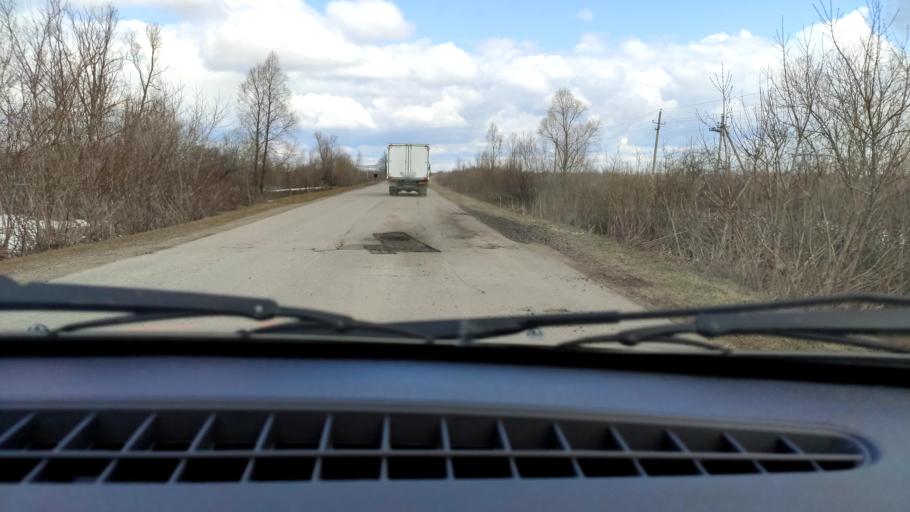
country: RU
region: Bashkortostan
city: Kudeyevskiy
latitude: 54.8322
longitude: 56.7929
